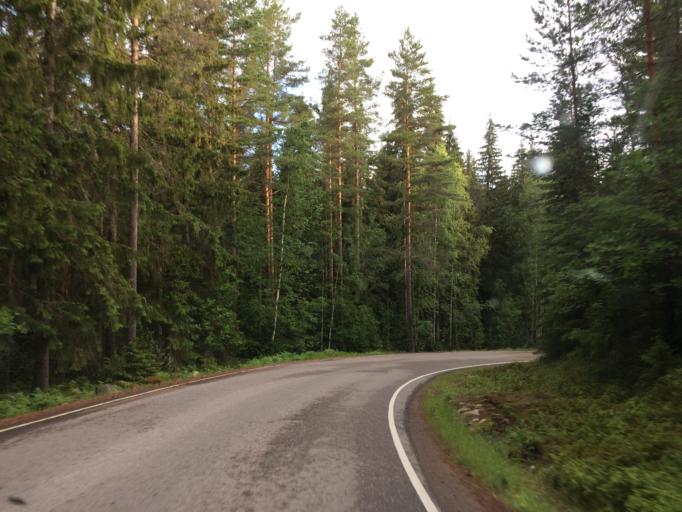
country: FI
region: Haeme
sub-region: Haemeenlinna
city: Janakkala
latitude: 60.8630
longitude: 24.5500
